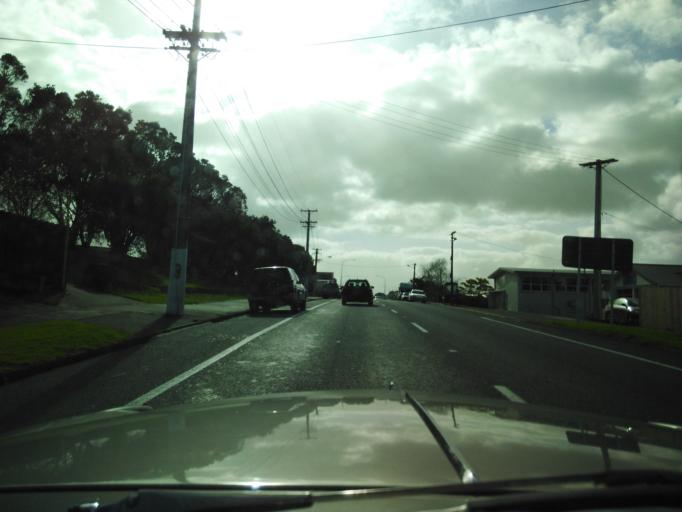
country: NZ
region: Auckland
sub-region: Auckland
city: Wellsford
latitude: -36.2984
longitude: 174.5239
